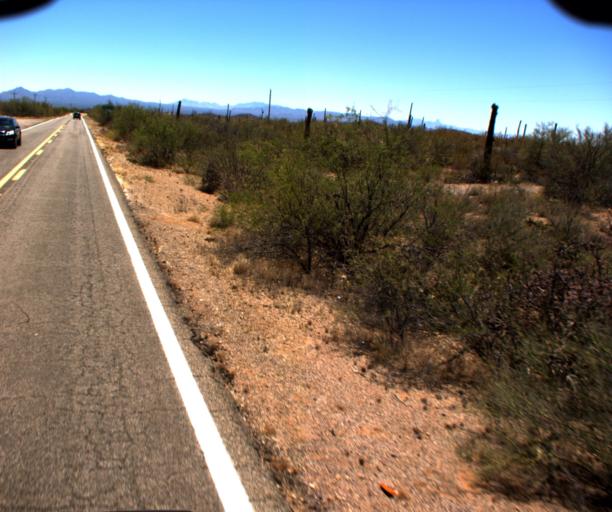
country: US
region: Arizona
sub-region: Pima County
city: Sells
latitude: 32.1688
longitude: -112.1355
